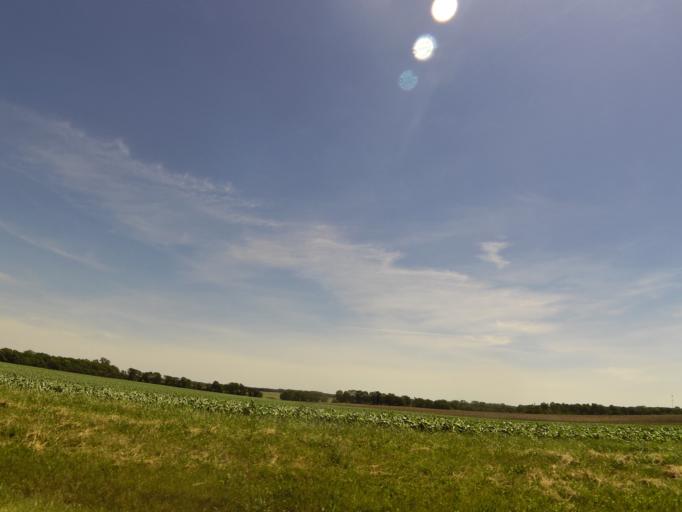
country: US
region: Illinois
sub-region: Vermilion County
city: Rossville
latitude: 40.2777
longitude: -87.6553
